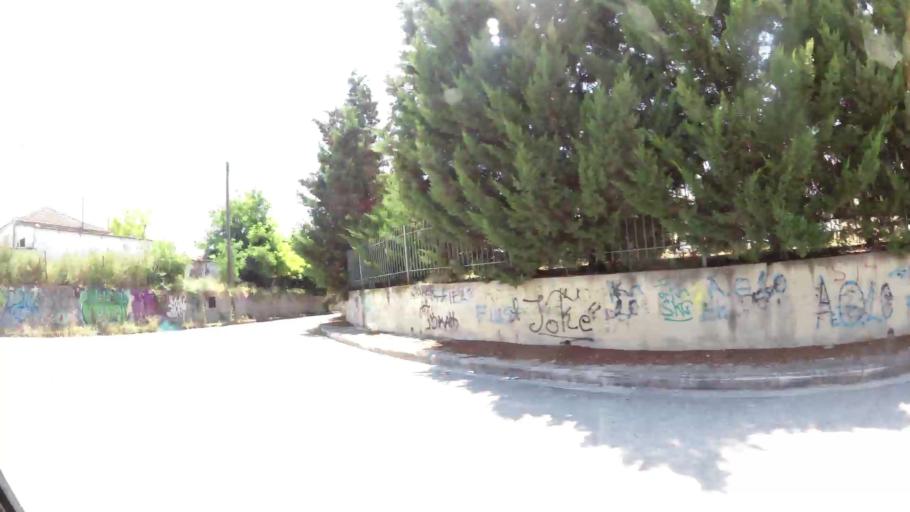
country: GR
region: Central Macedonia
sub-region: Nomos Thessalonikis
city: Trilofos
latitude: 40.4702
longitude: 22.9731
